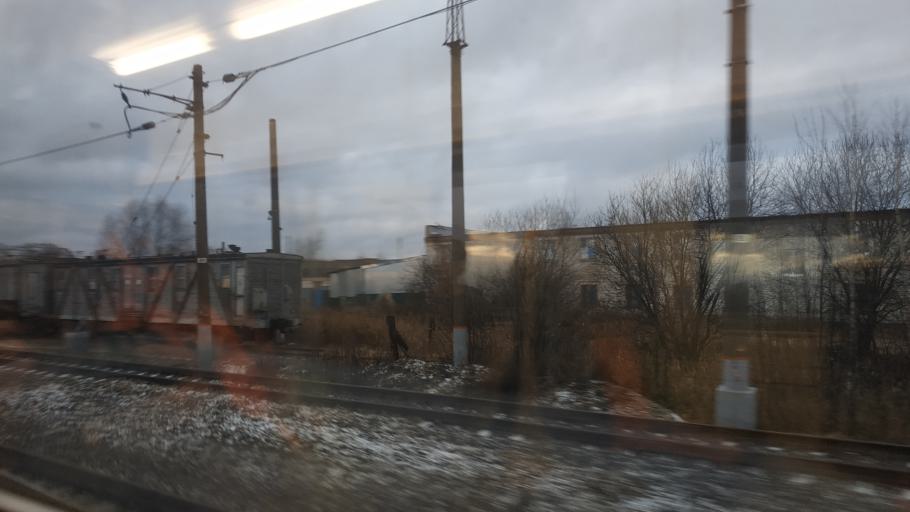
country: RU
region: Moskovskaya
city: Taldom
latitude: 56.7184
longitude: 37.5339
